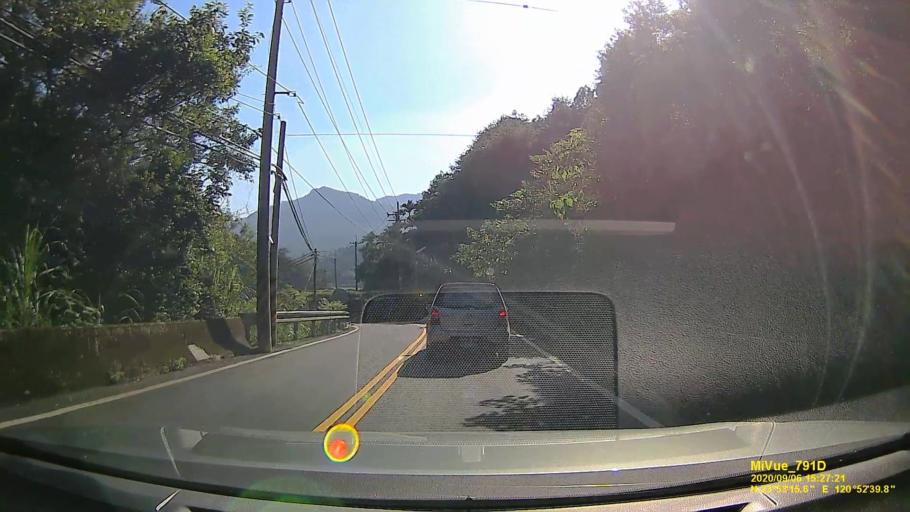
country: TW
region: Taiwan
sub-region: Nantou
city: Puli
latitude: 23.8876
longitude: 120.8777
